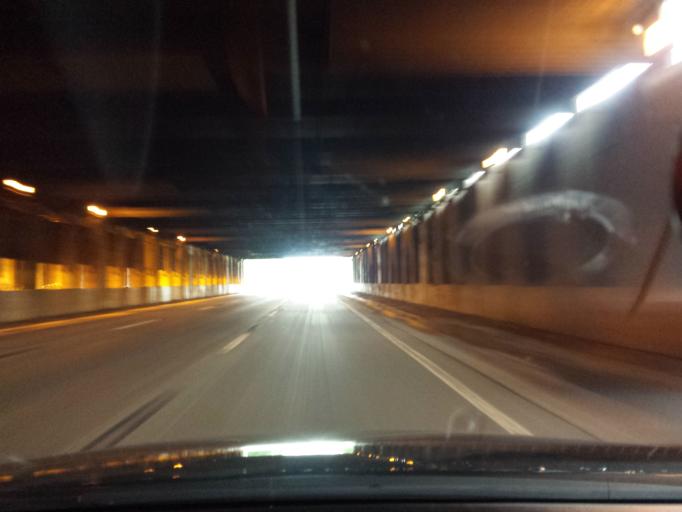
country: US
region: New York
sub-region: Westchester County
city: Larchmont
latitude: 40.9344
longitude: -73.7589
